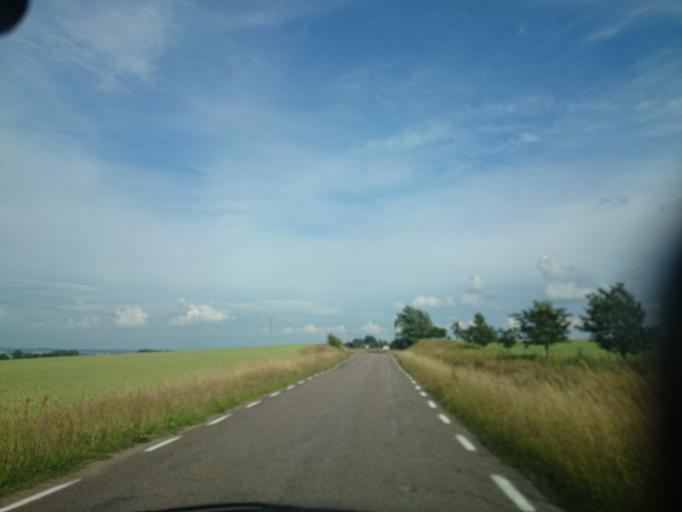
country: SE
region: Skane
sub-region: Lunds Kommun
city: Lund
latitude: 55.7476
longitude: 13.2570
